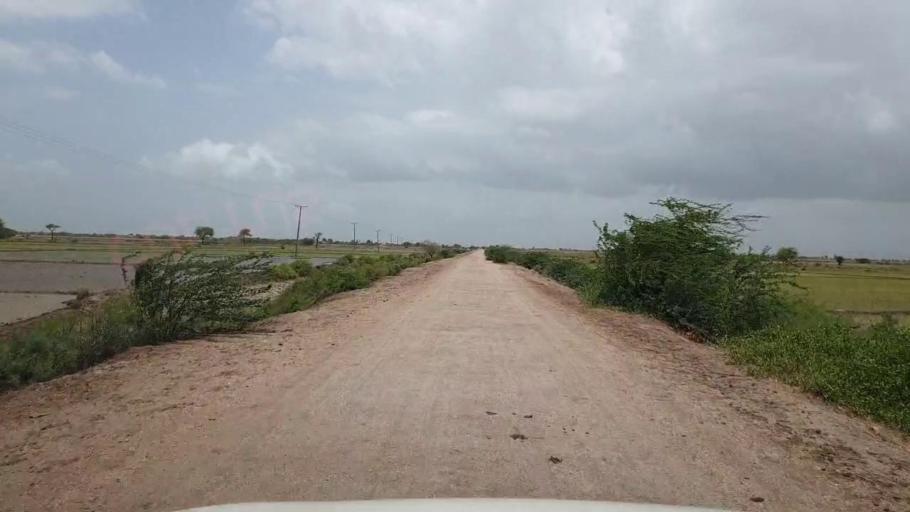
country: PK
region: Sindh
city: Kario
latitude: 24.6985
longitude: 68.6360
